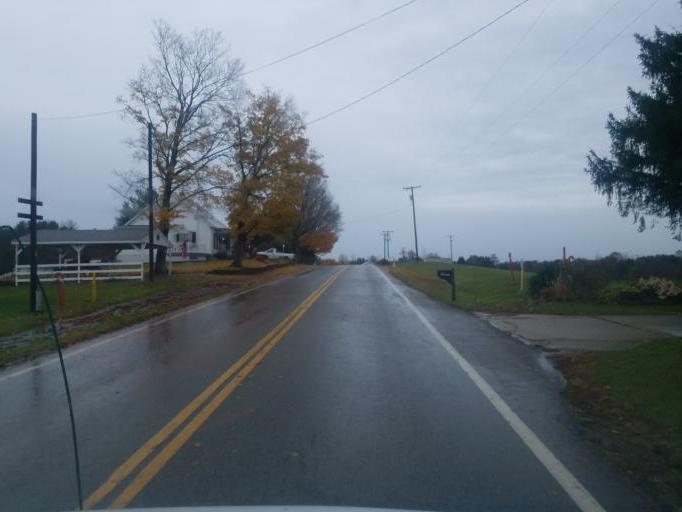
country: US
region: Ohio
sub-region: Morgan County
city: McConnelsville
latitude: 39.4832
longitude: -81.8685
